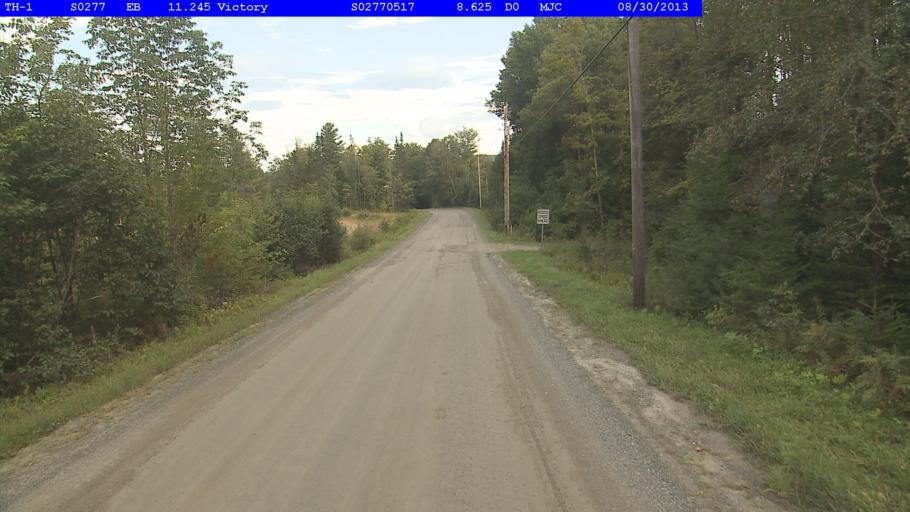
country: US
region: Vermont
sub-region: Essex County
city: Guildhall
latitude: 44.5687
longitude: -71.7633
